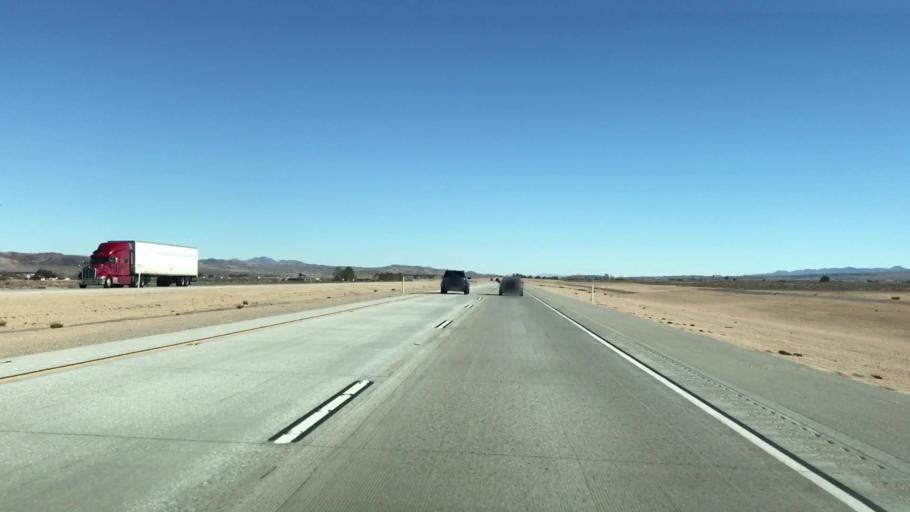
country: US
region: California
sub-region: San Bernardino County
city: Lenwood
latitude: 34.9135
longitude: -117.2088
